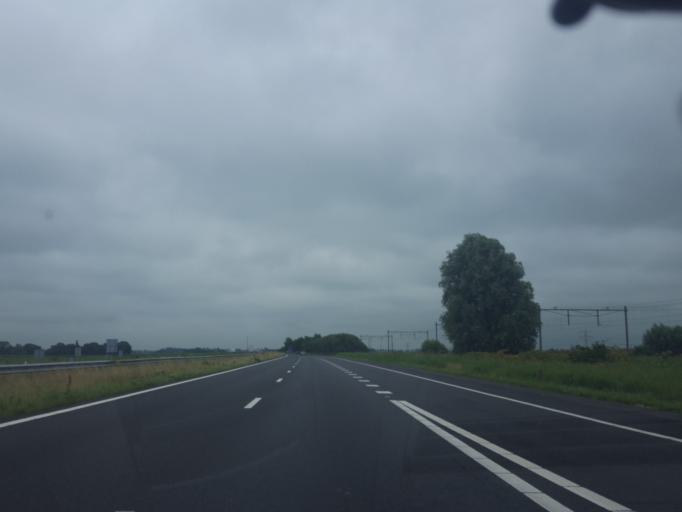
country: NL
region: Friesland
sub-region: Gemeente Leeuwarden
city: Wirdum
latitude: 53.1429
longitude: 5.7969
